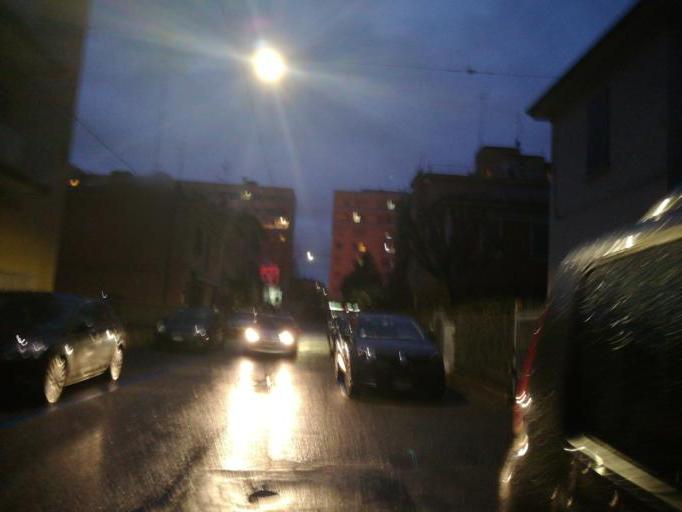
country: IT
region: Emilia-Romagna
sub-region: Provincia di Bologna
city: Progresso
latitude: 44.5471
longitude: 11.3579
